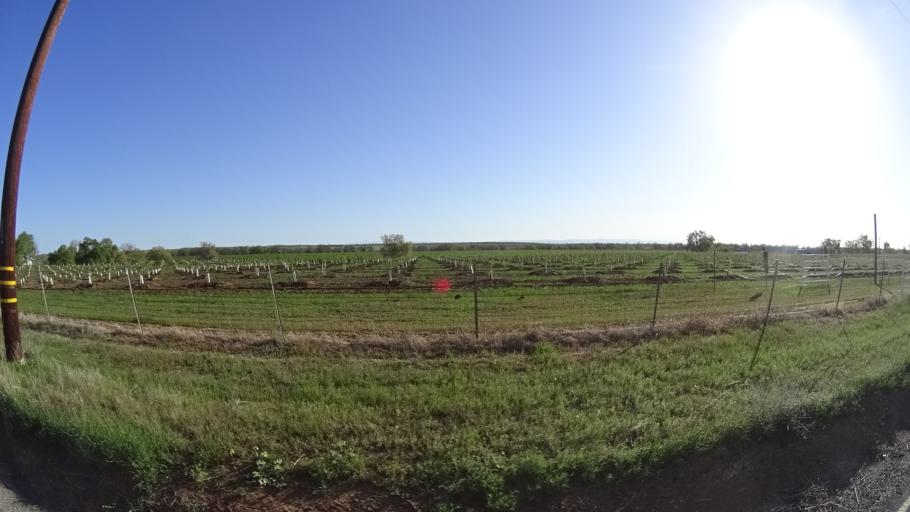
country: US
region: California
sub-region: Glenn County
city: Orland
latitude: 39.8063
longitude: -122.3294
